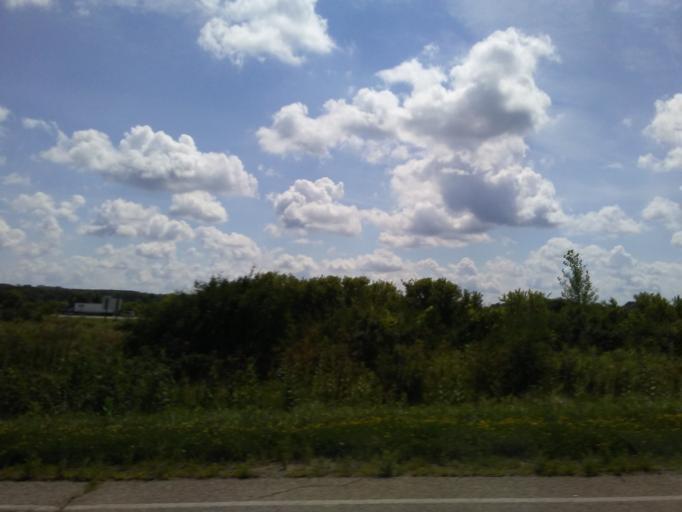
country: US
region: Wisconsin
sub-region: Dane County
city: Verona
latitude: 42.9977
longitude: -89.5029
